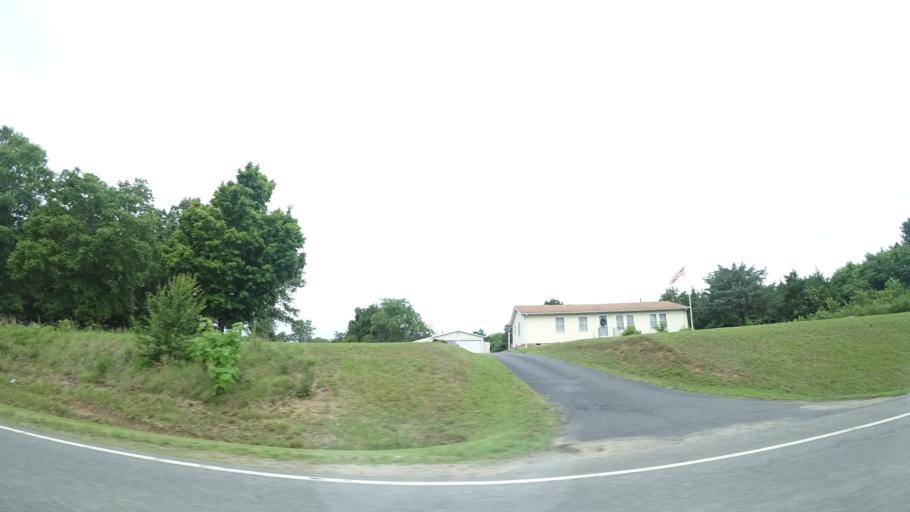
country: US
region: Virginia
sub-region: Spotsylvania County
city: Spotsylvania
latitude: 38.1443
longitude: -77.7177
